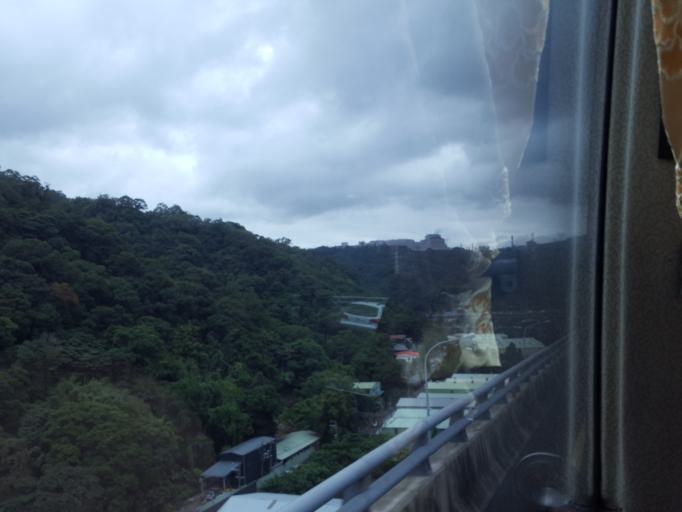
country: TW
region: Taipei
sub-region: Taipei
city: Banqiao
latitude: 25.0606
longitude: 121.3965
